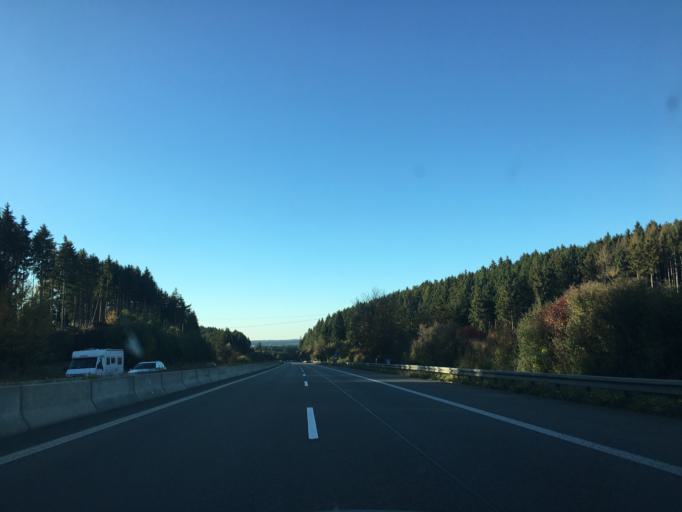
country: DE
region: Baden-Wuerttemberg
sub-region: Freiburg Region
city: Trossingen
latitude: 48.0636
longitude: 8.6151
